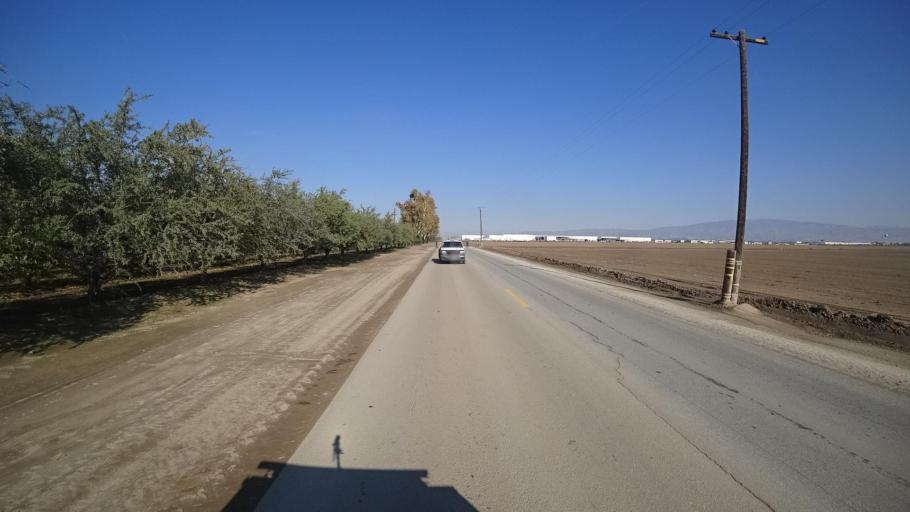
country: US
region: California
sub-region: Kern County
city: Arvin
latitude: 35.2444
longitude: -118.8606
